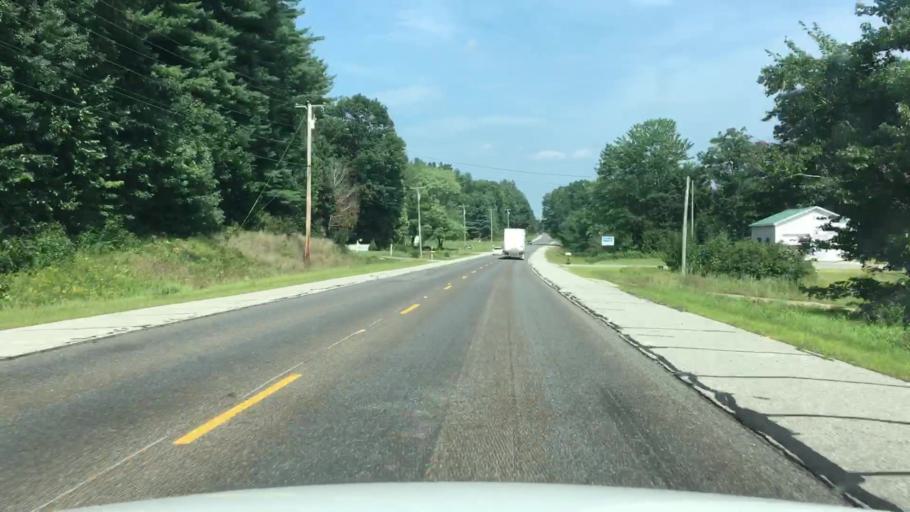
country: US
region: Maine
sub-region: Androscoggin County
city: Turner
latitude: 44.3136
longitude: -70.2641
